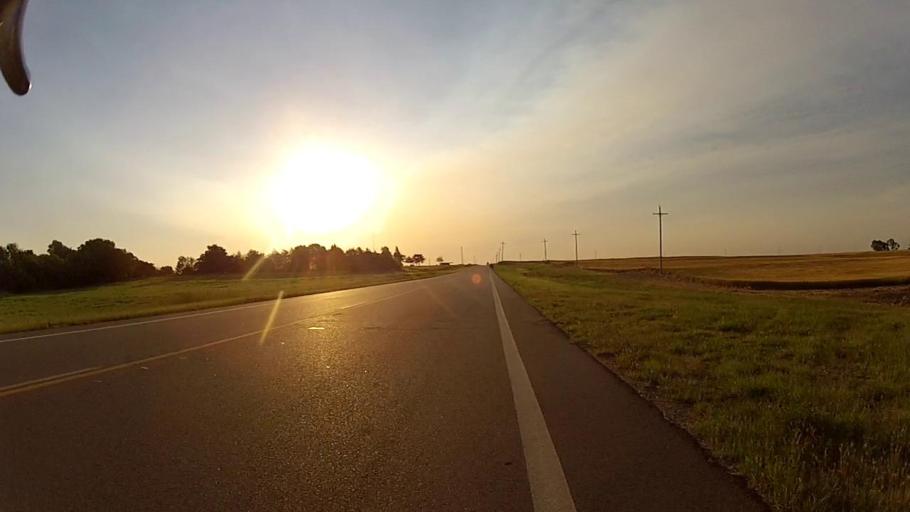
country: US
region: Kansas
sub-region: Harper County
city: Anthony
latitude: 37.1527
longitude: -97.9346
